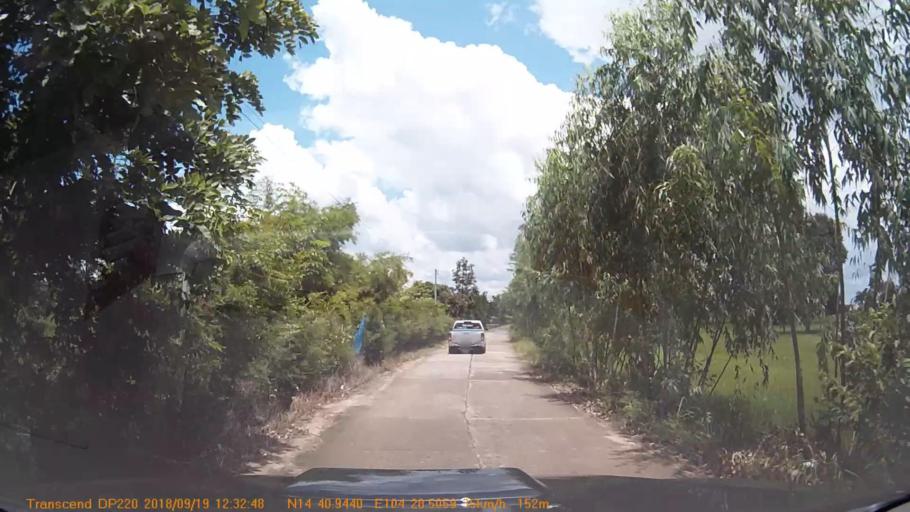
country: TH
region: Sisaket
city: Khun Han
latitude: 14.6826
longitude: 104.4753
